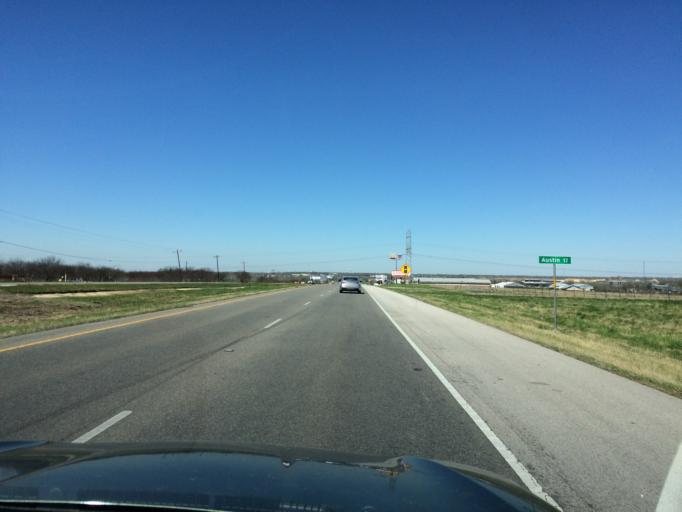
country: US
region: Texas
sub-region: Travis County
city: Garfield
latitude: 30.1722
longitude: -97.5212
